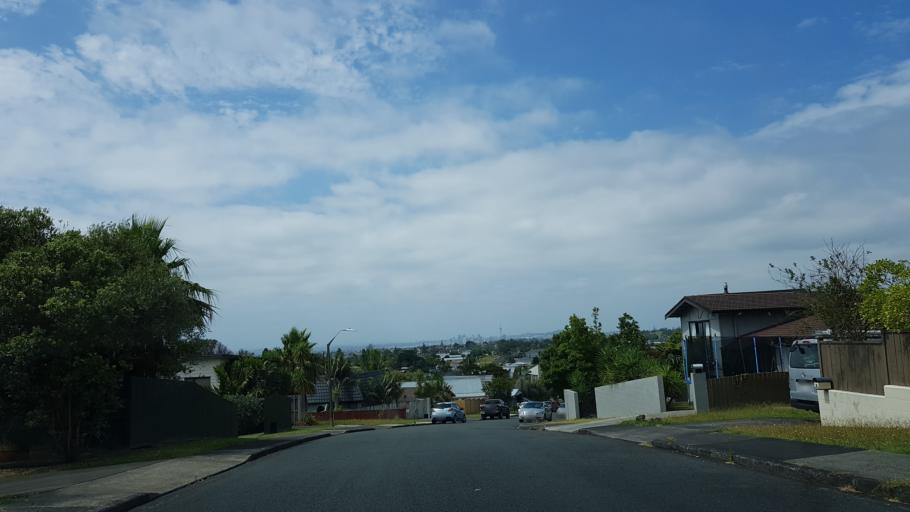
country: NZ
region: Auckland
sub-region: Auckland
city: Rothesay Bay
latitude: -36.7665
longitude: 174.7171
